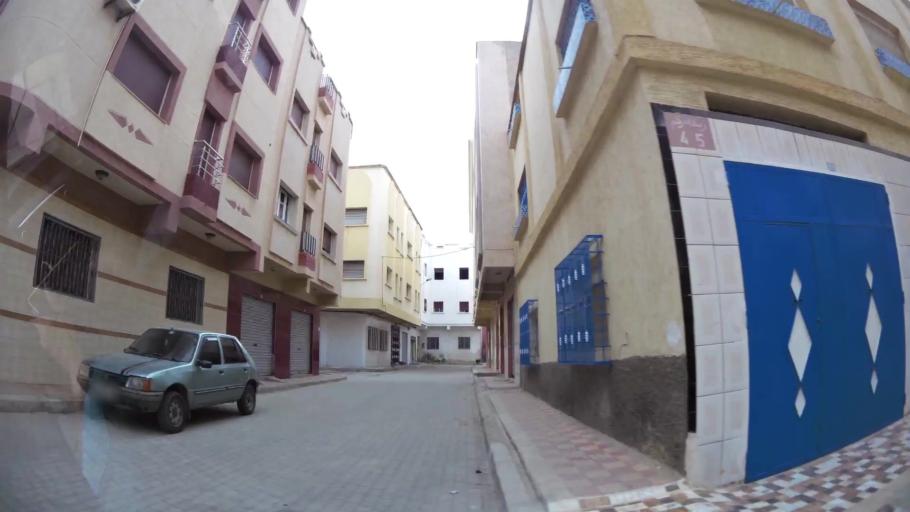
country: MA
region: Oriental
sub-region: Nador
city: Nador
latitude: 35.1617
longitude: -2.9335
